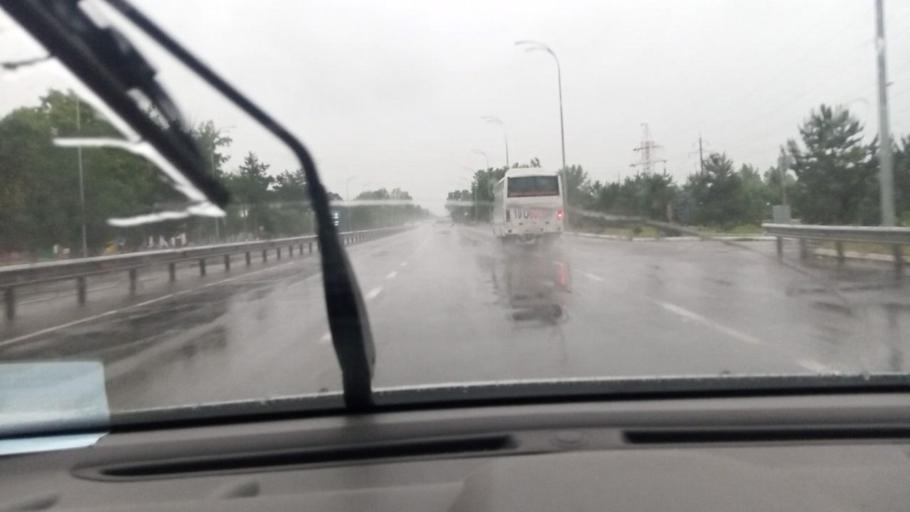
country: UZ
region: Toshkent Shahri
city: Bektemir
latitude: 41.2552
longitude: 69.3826
